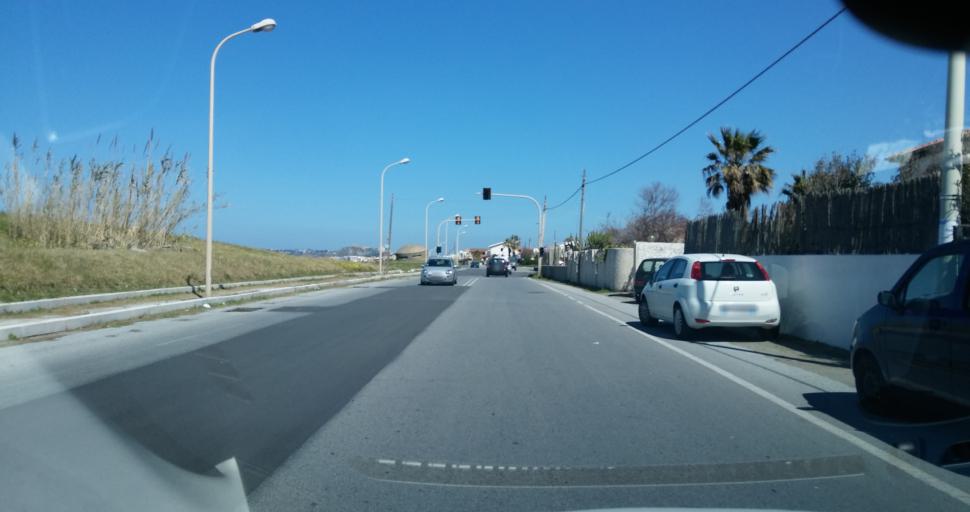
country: IT
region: Sicily
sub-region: Messina
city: Milazzo
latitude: 38.1931
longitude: 15.2187
